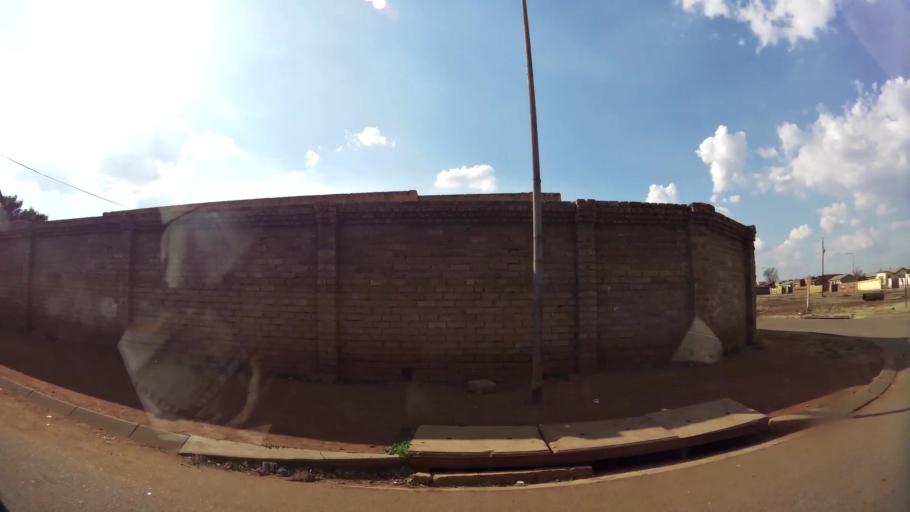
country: ZA
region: Gauteng
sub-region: City of Johannesburg Metropolitan Municipality
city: Soweto
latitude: -26.2194
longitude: 27.8612
